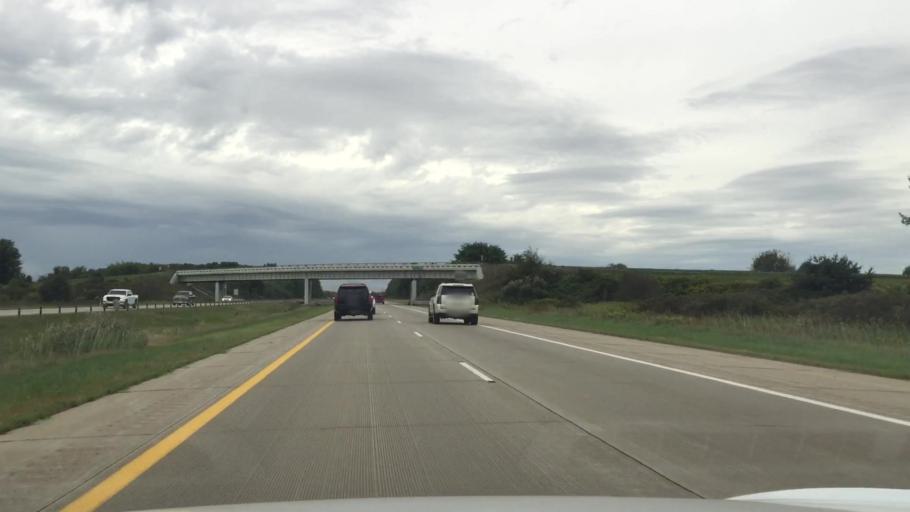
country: US
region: Michigan
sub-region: Macomb County
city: Richmond
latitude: 42.7656
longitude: -82.6916
